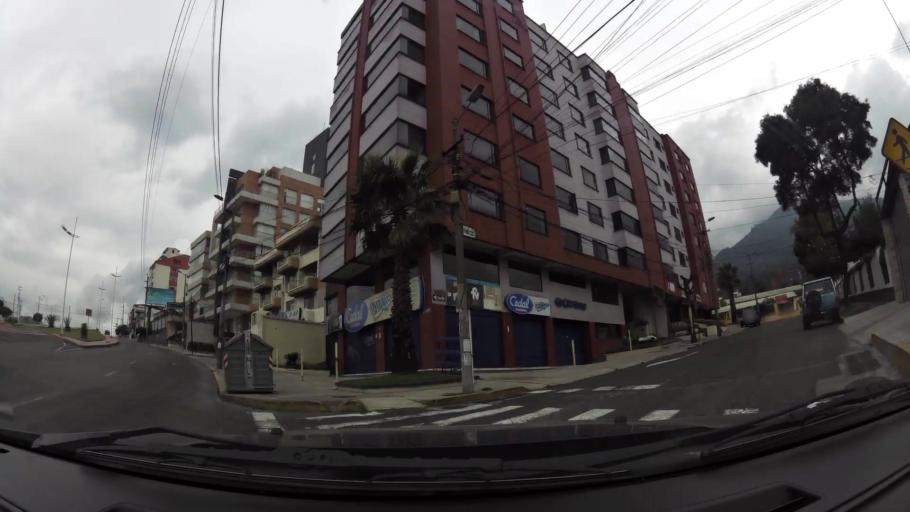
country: EC
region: Pichincha
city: Quito
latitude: -0.1742
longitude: -78.4935
